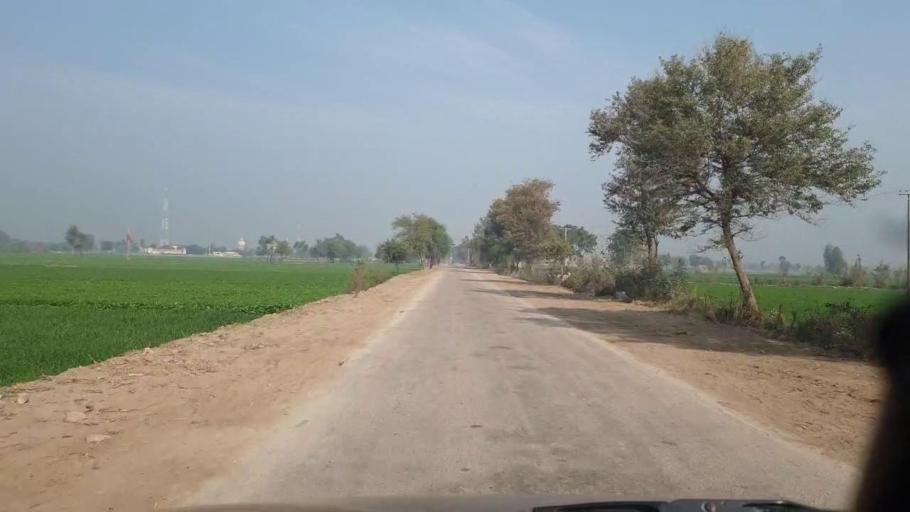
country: PK
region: Sindh
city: Shahdadpur
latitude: 26.0198
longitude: 68.5463
